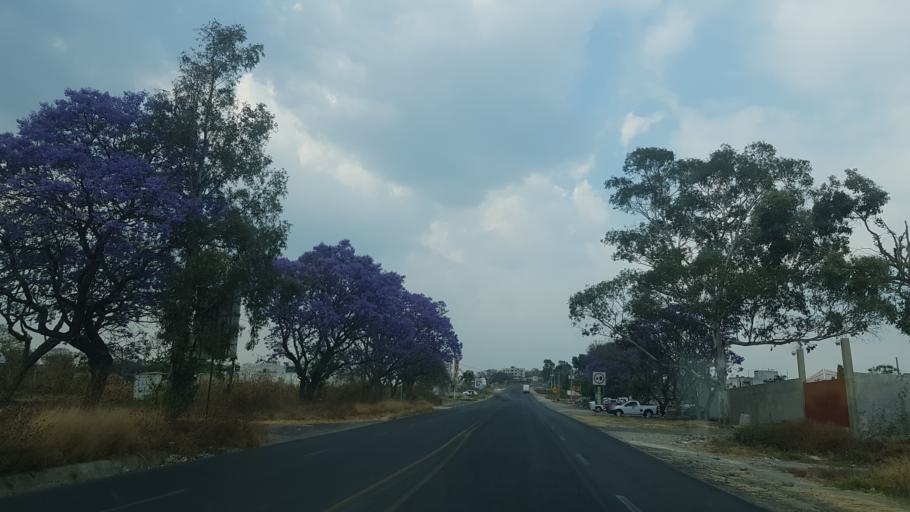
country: MX
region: Puebla
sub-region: Santa Isabel Cholula
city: Santa Ana Acozautla
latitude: 18.9605
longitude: -98.3860
